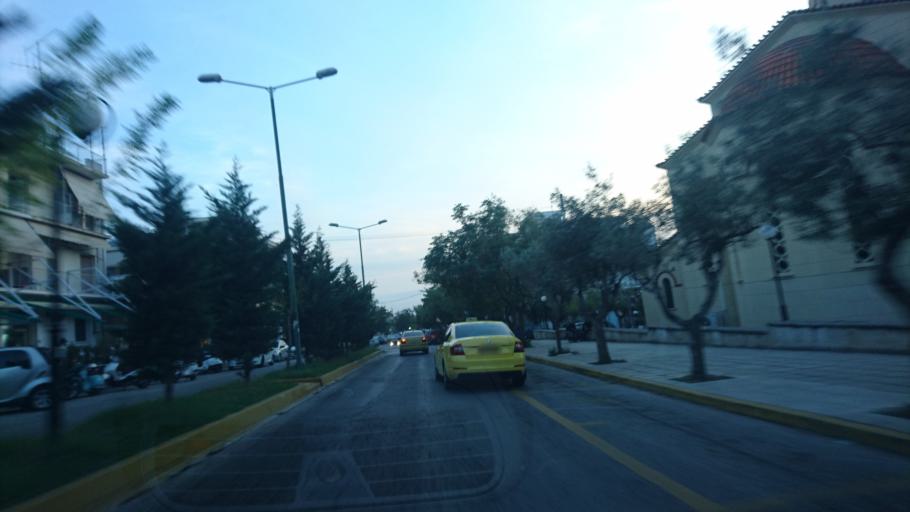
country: GR
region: Attica
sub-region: Nomarchia Athinas
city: Ilioupoli
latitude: 37.9339
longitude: 23.7572
